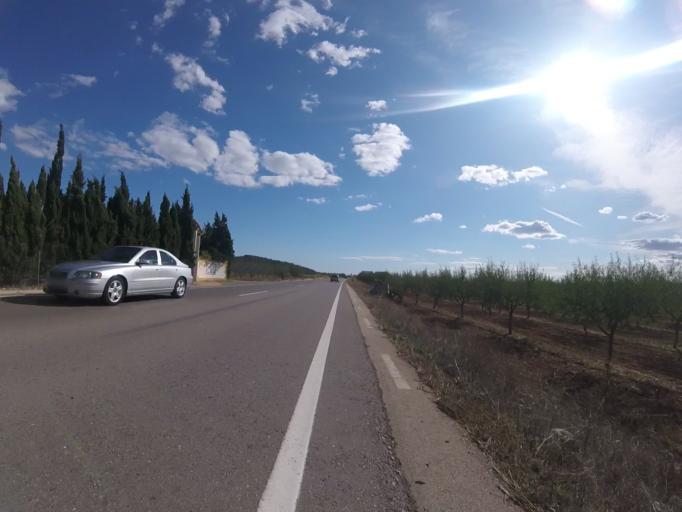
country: ES
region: Valencia
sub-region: Provincia de Castello
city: Alcala de Xivert
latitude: 40.2624
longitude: 0.2431
